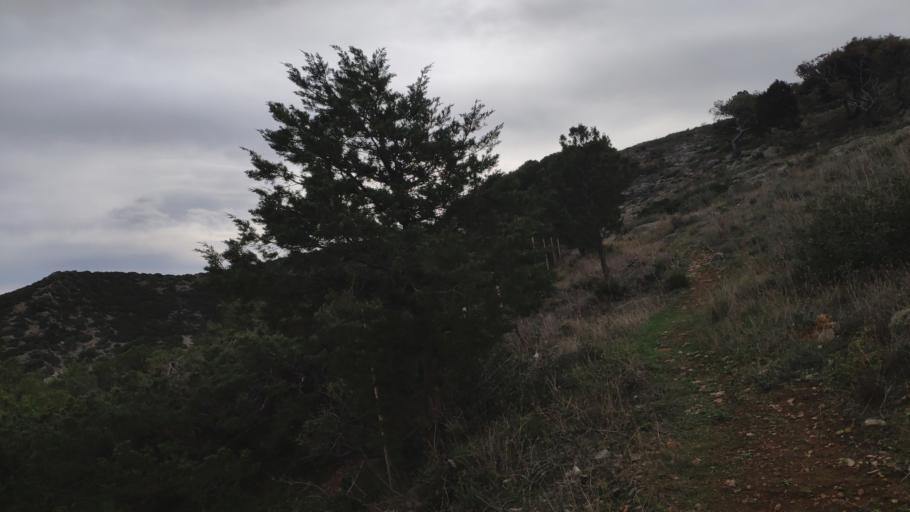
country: GR
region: Attica
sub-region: Nomarchia Anatolikis Attikis
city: Limin Mesoyaias
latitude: 37.9090
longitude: 24.0393
